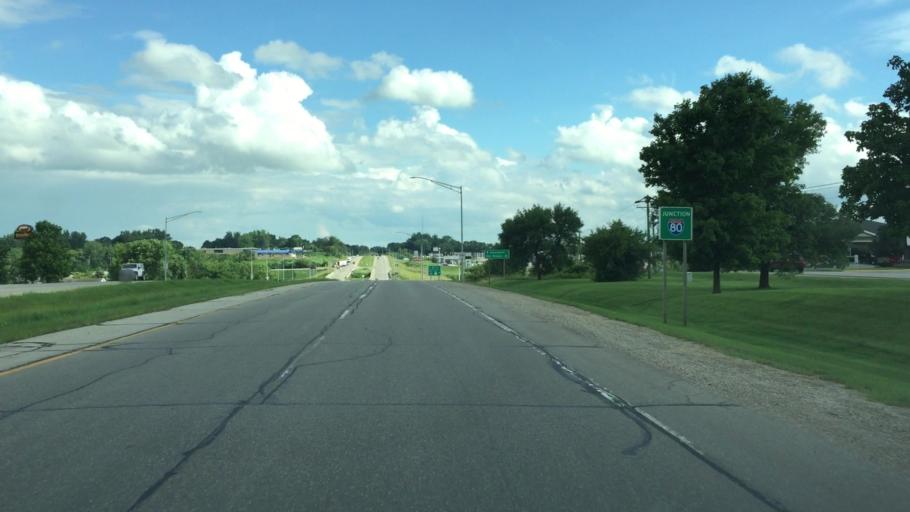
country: US
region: Iowa
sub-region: Jasper County
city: Newton
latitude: 41.6880
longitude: -93.0776
